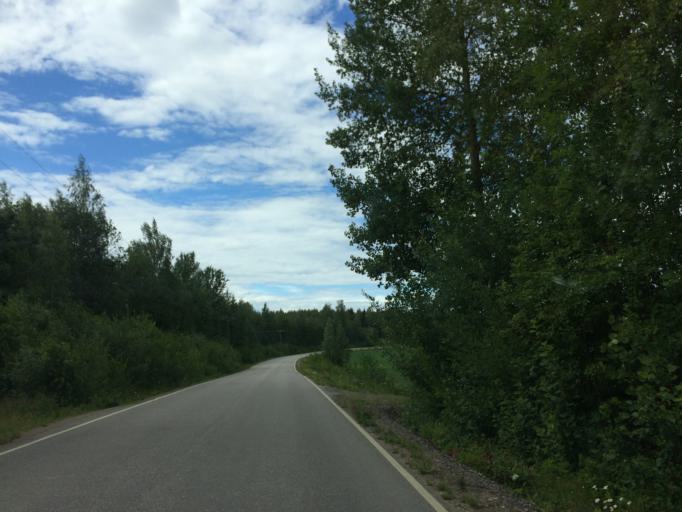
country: FI
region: Haeme
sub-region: Haemeenlinna
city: Tervakoski
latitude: 60.8301
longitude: 24.5961
